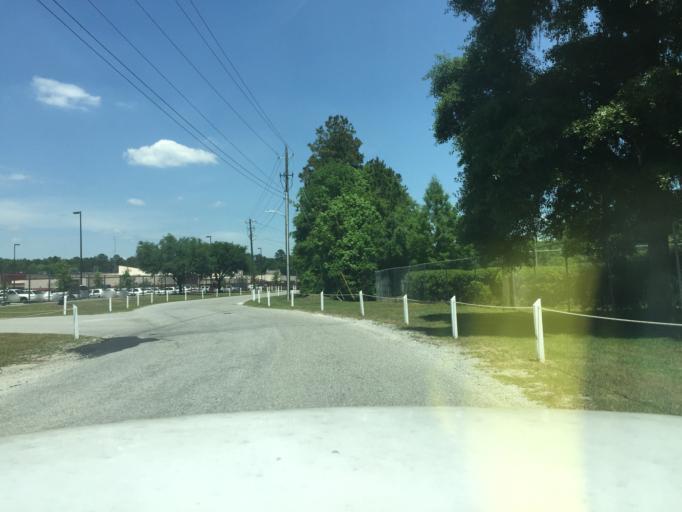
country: US
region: Georgia
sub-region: Chatham County
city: Garden City
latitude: 32.0645
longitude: -81.1665
